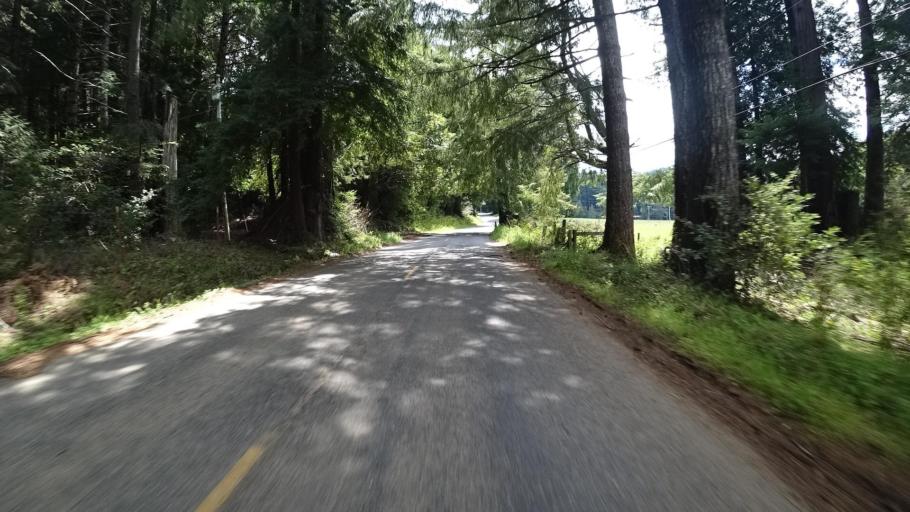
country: US
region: California
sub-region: Humboldt County
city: Redway
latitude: 40.0305
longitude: -123.9501
